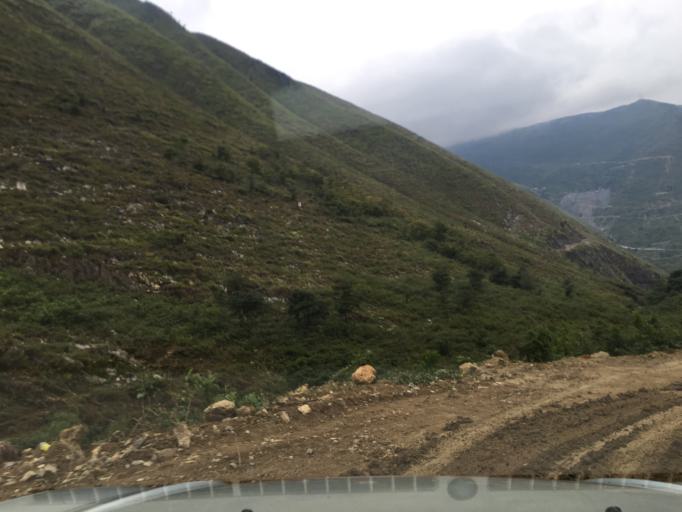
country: CN
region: Guizhou Sheng
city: Liupanshui
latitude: 25.9647
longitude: 105.2383
